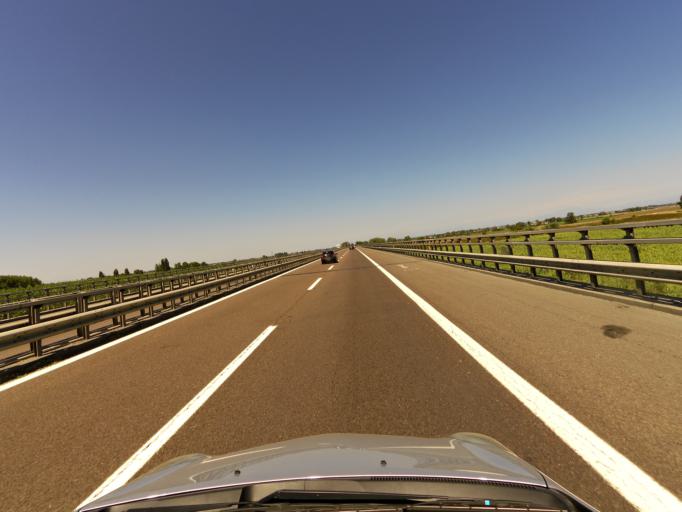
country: IT
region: Lombardy
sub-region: Provincia di Mantova
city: San Biagio
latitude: 45.0527
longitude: 10.8460
